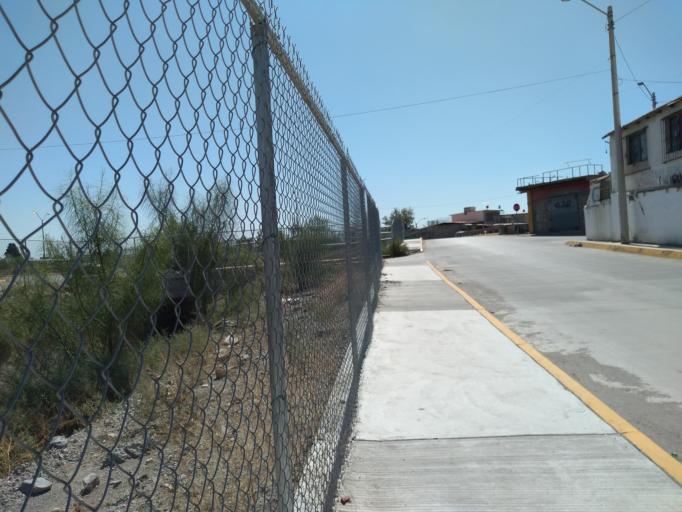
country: US
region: Texas
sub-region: El Paso County
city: El Paso
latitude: 31.7499
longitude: -106.4958
